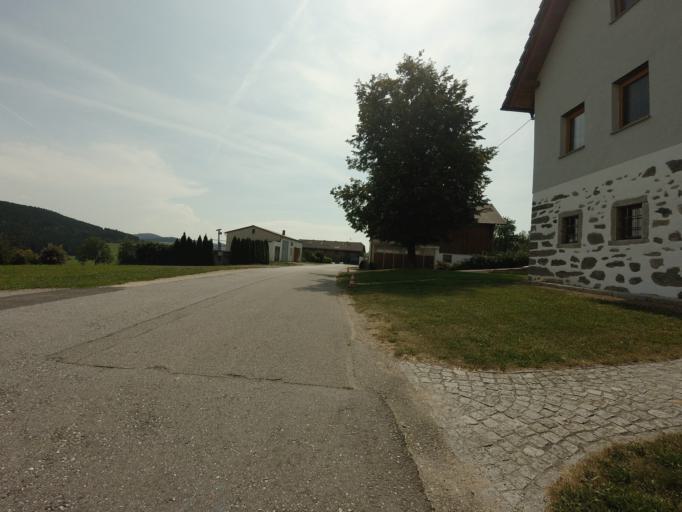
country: AT
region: Upper Austria
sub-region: Politischer Bezirk Urfahr-Umgebung
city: Schenkenfelden
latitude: 48.5220
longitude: 14.3605
